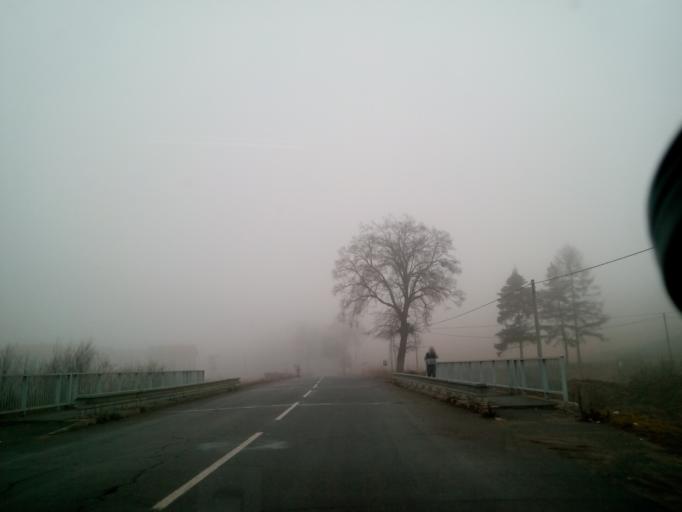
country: SK
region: Presovsky
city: Spisske Podhradie
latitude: 48.9706
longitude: 20.7831
